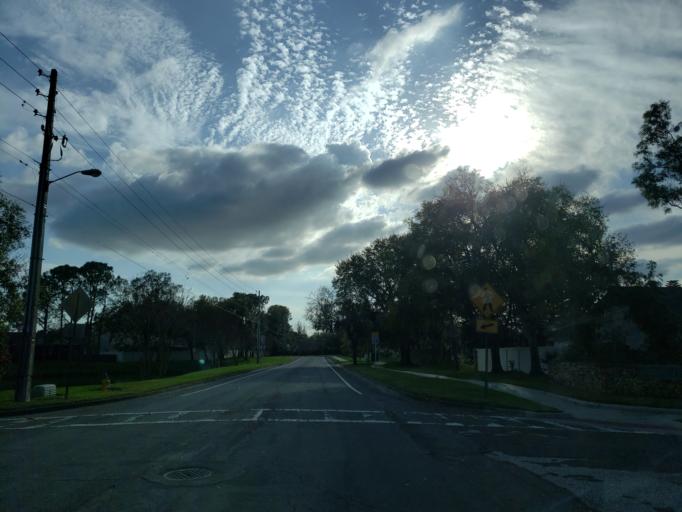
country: US
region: Florida
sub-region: Hillsborough County
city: Riverview
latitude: 27.9057
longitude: -82.3242
